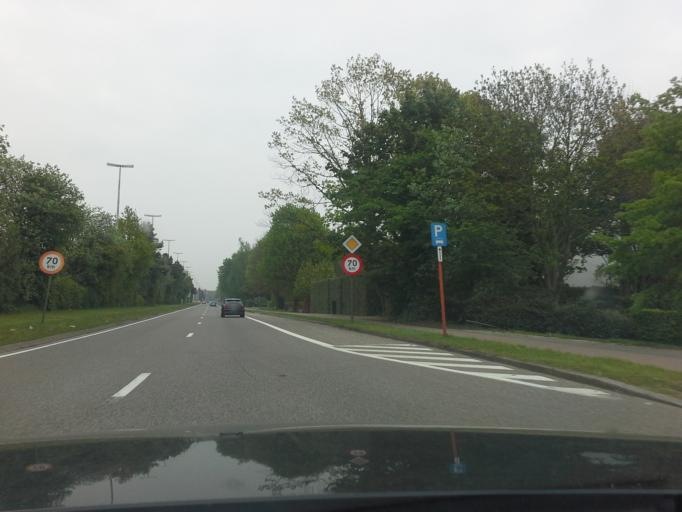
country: BE
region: Flanders
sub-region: Provincie Antwerpen
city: Turnhout
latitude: 51.3130
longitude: 4.9523
